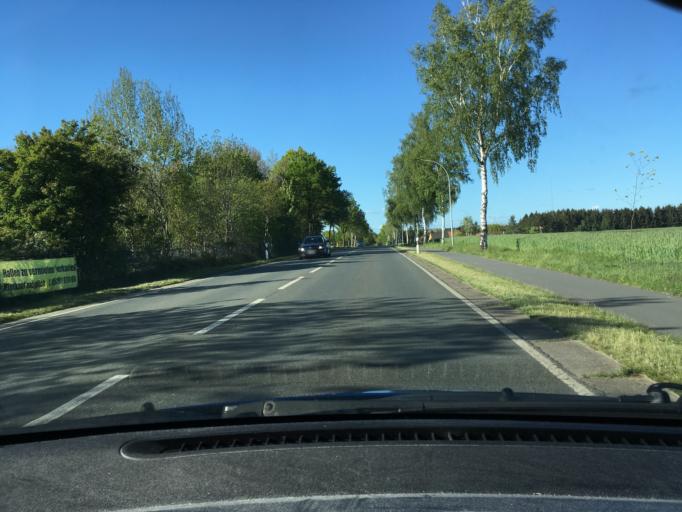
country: DE
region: Lower Saxony
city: Soltau
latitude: 53.0046
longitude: 9.8407
